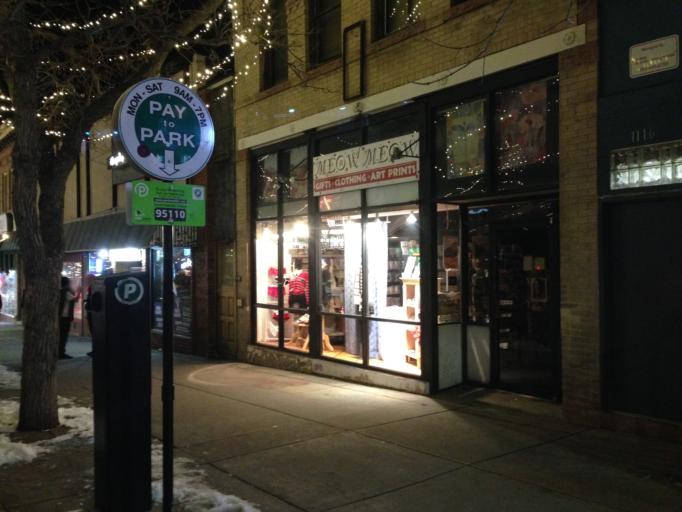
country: US
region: Colorado
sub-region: Boulder County
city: Boulder
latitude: 40.0077
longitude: -105.2761
